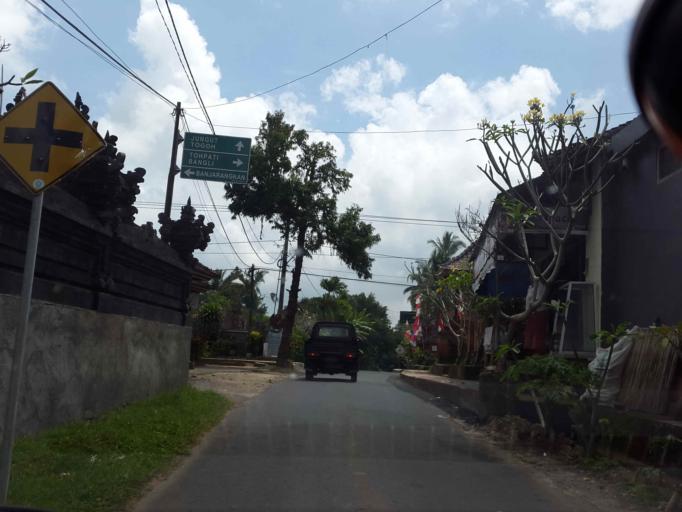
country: ID
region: Bali
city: Banjar Kelodan
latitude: -8.4768
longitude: 115.3762
